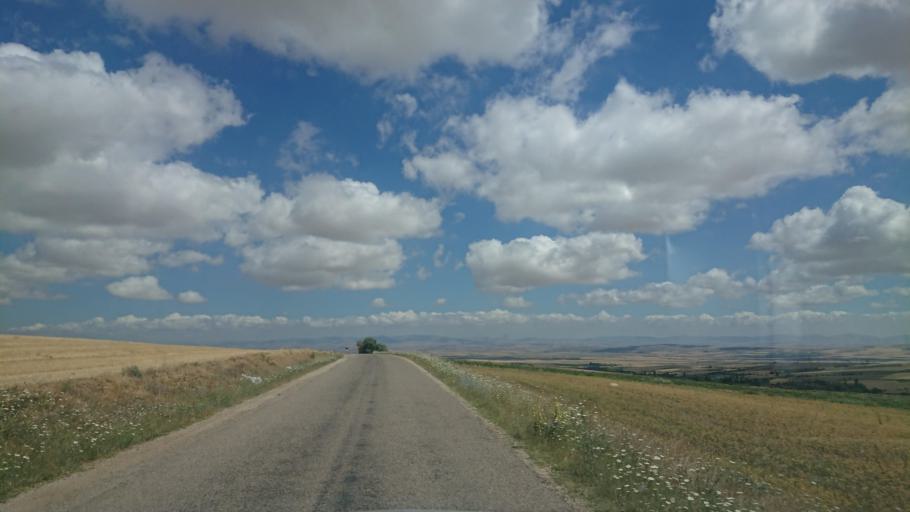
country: TR
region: Aksaray
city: Agacoren
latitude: 38.8463
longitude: 33.9492
